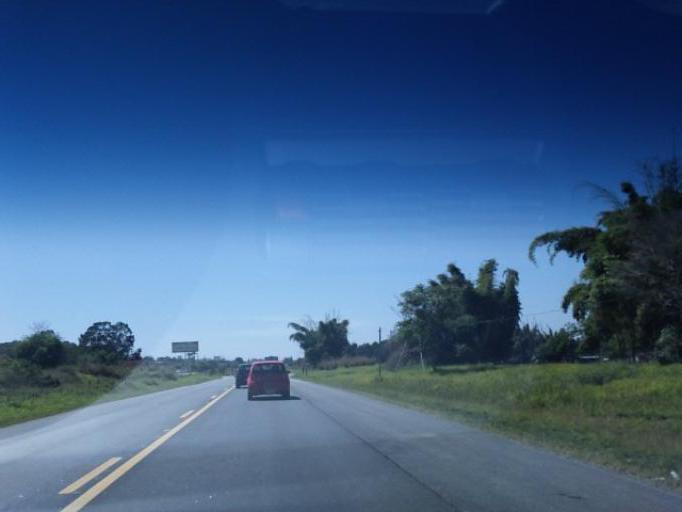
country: BR
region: Sao Paulo
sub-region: Tremembe
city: Tremembe
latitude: -22.9468
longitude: -45.6094
